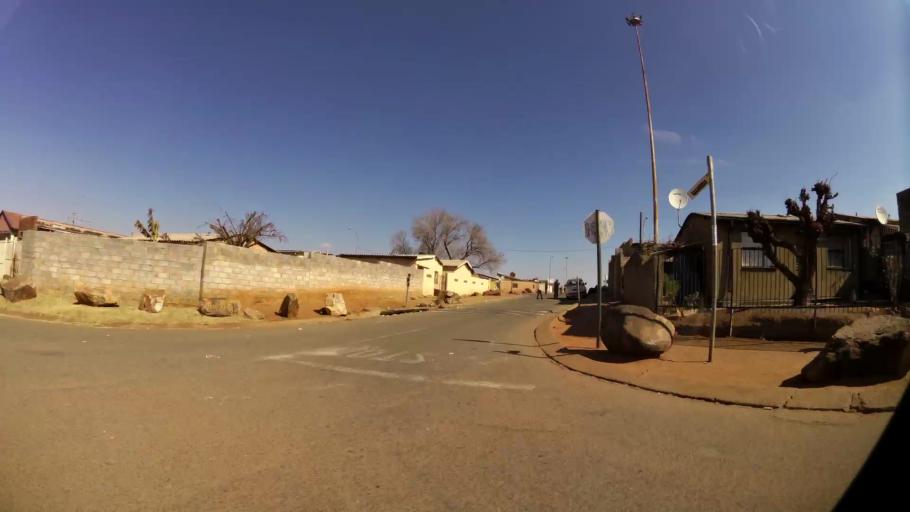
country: ZA
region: Gauteng
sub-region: City of Johannesburg Metropolitan Municipality
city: Soweto
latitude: -26.2349
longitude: 27.8838
